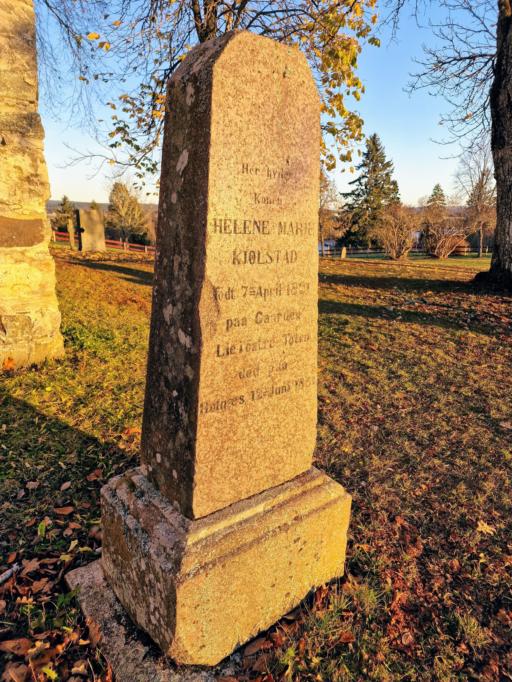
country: NO
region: Akershus
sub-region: Nes
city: Arnes
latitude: 60.1489
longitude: 11.4568
